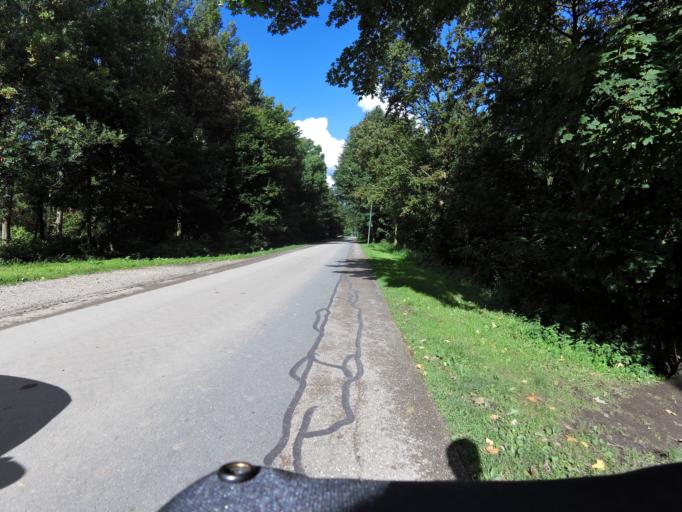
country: NL
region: South Holland
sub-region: Gemeente Vlaardingen
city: Vlaardingen
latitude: 51.9244
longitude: 4.3377
